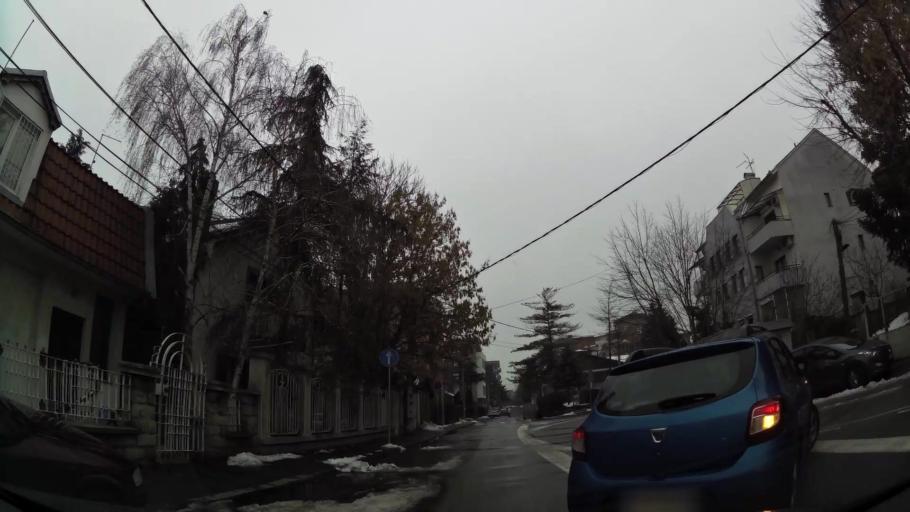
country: RS
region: Central Serbia
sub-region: Belgrade
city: Vozdovac
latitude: 44.7837
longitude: 20.4743
